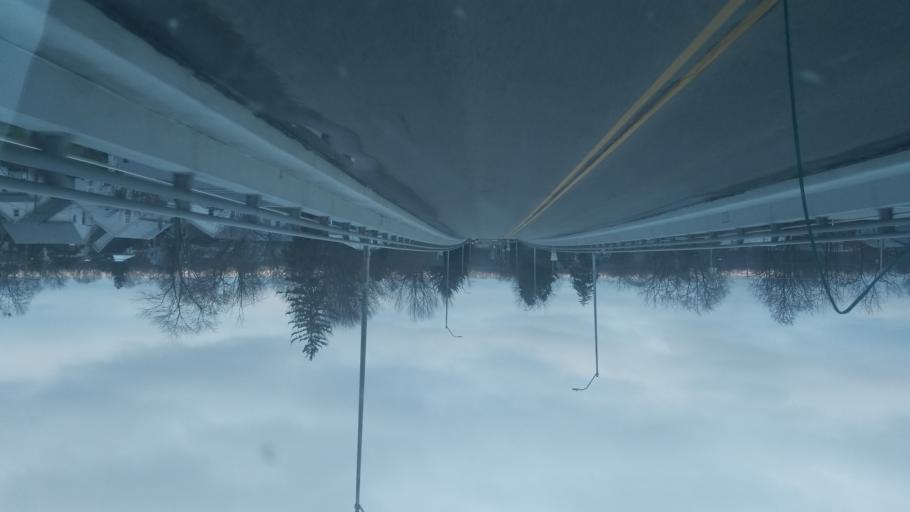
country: US
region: Ohio
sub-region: Crawford County
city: Galion
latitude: 40.7351
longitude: -82.7830
